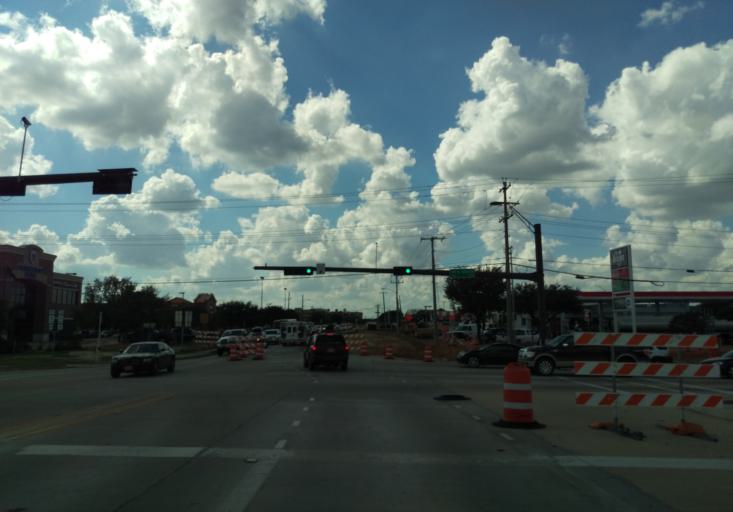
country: US
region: Texas
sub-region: Brazos County
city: College Station
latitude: 30.5846
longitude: -96.2856
